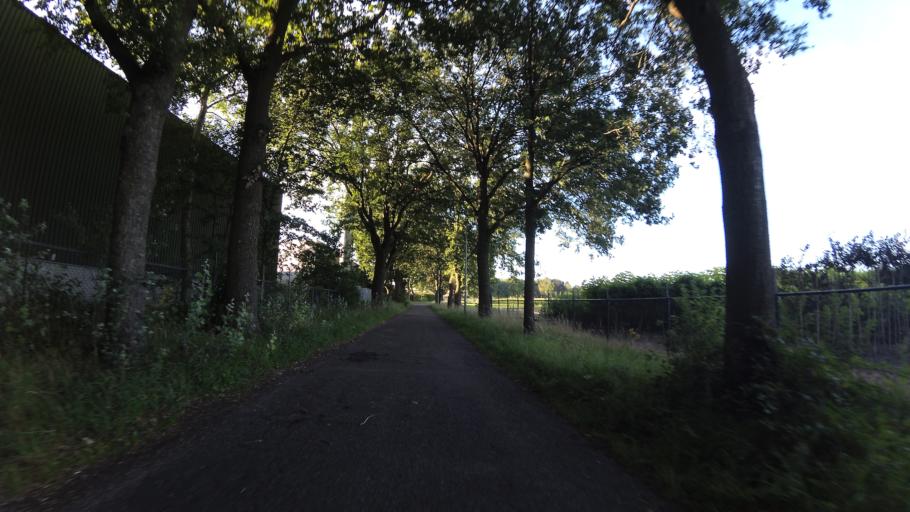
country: NL
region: North Brabant
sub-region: Gemeente Breda
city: Hoge Vucht
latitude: 51.6191
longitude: 4.8262
